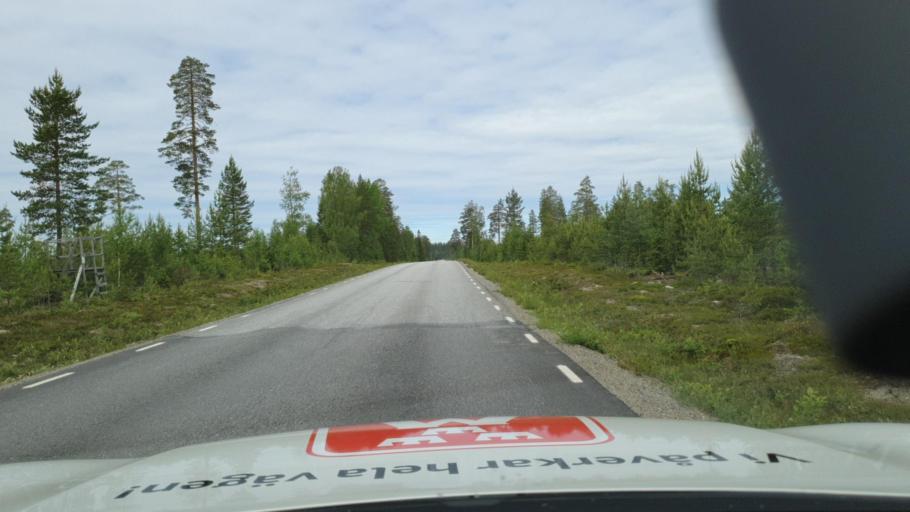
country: SE
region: Vaesterbotten
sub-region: Skelleftea Kommun
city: Langsele
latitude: 64.5350
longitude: 20.2937
